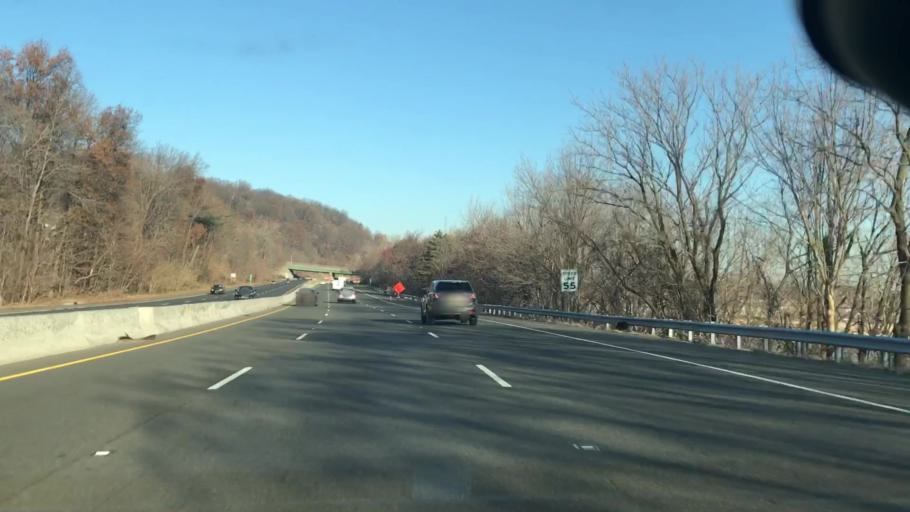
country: US
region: New Jersey
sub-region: Passaic County
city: Paterson
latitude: 40.8947
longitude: -74.1685
